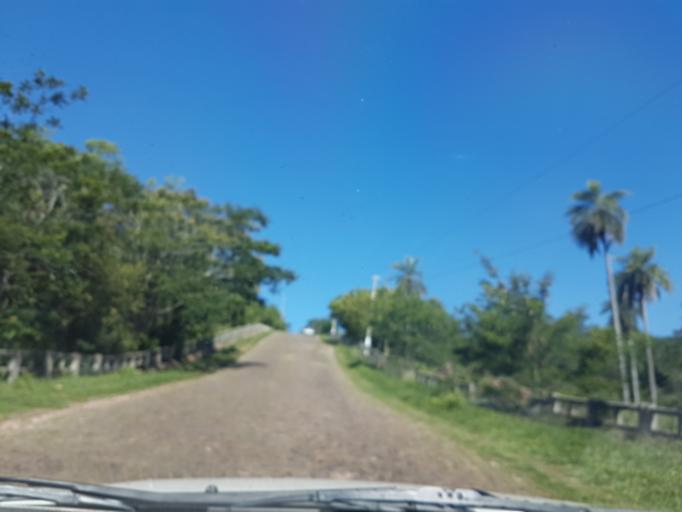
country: PY
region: Cordillera
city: Atyra
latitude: -25.2792
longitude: -57.1509
